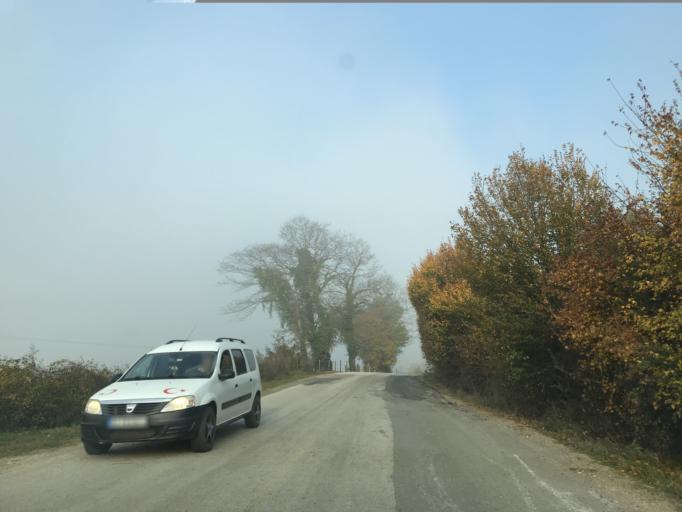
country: TR
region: Duzce
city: Cumayeri
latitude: 40.8973
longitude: 30.9523
